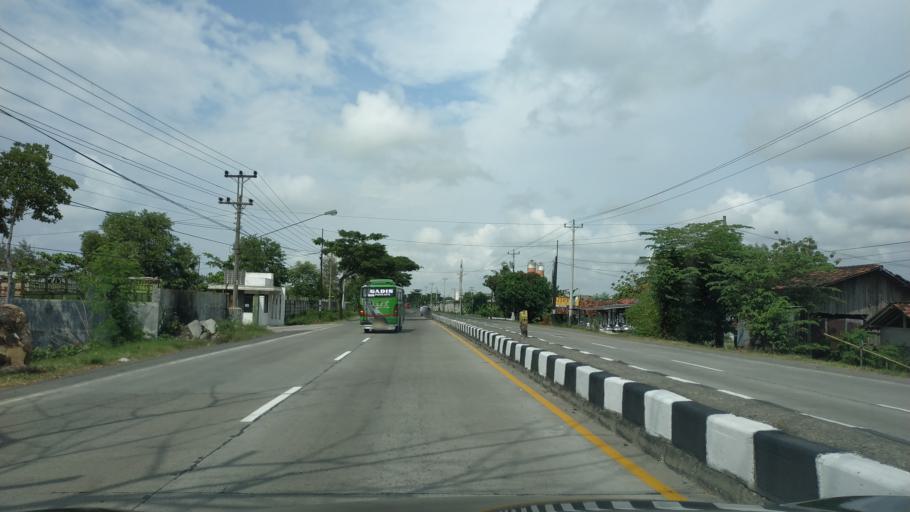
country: ID
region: Central Java
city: Tarub
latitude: -6.8722
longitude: 109.2437
